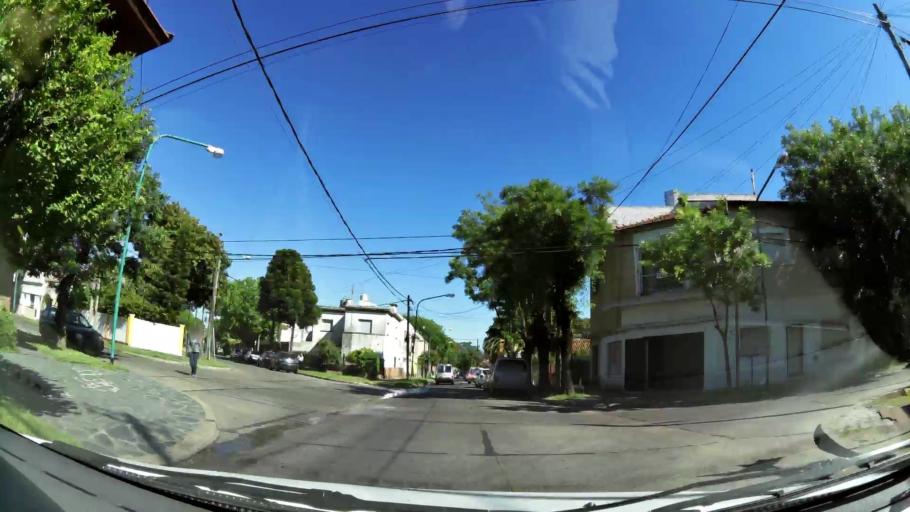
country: AR
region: Buenos Aires
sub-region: Partido de General San Martin
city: General San Martin
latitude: -34.5438
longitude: -58.5048
